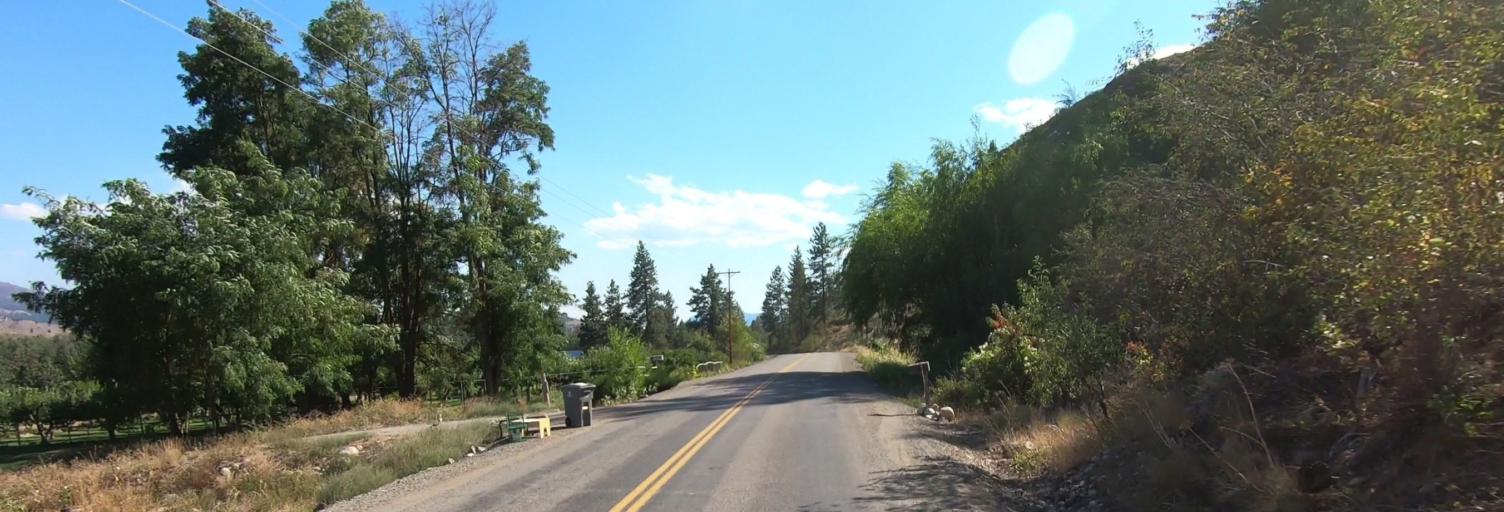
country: US
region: Washington
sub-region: Okanogan County
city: Brewster
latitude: 48.5270
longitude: -120.1920
